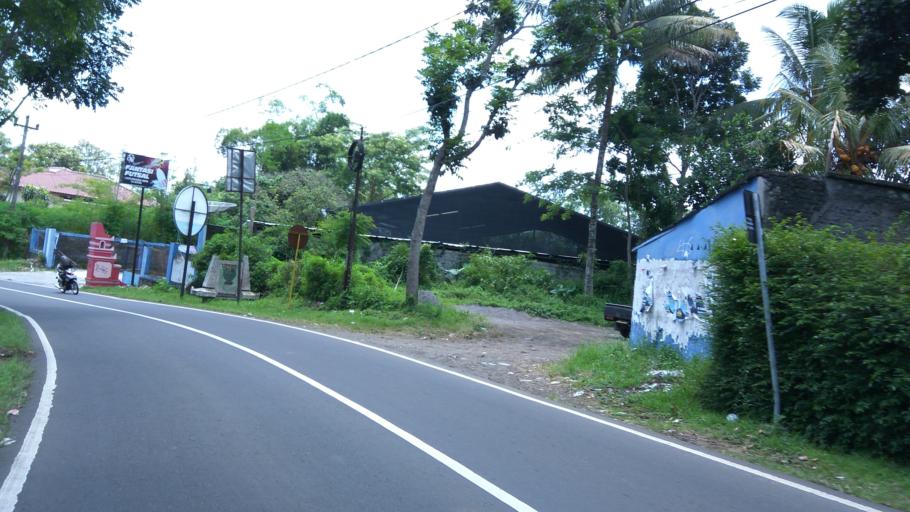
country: ID
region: Central Java
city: Ambarawa
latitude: -7.2516
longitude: 110.4005
